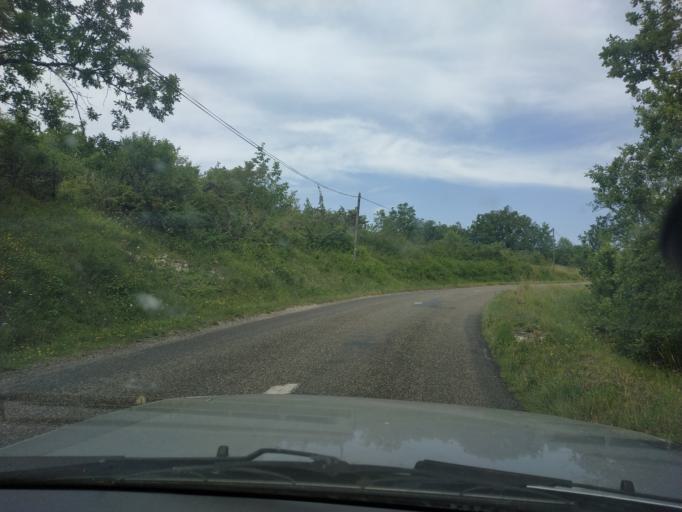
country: FR
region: Midi-Pyrenees
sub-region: Departement du Lot
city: Gramat
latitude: 44.6081
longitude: 1.6396
